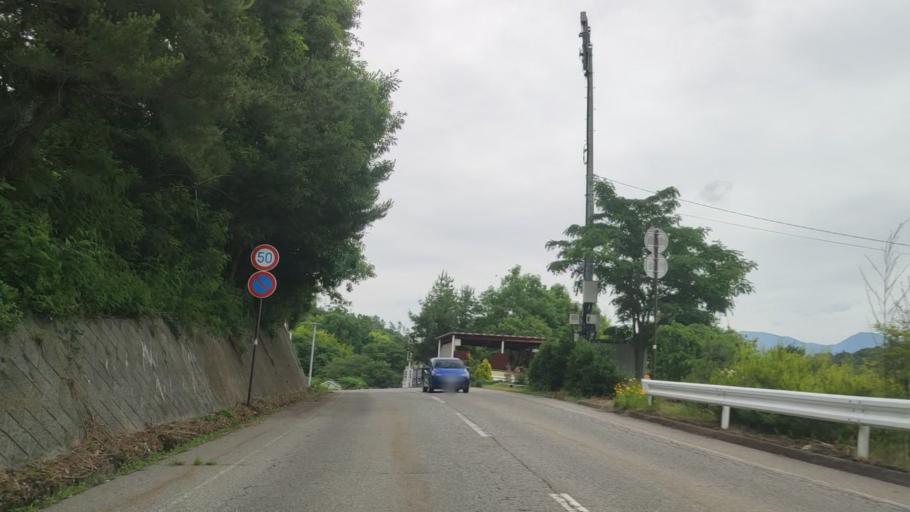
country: JP
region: Nagano
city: Kamimaruko
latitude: 36.3096
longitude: 138.3286
